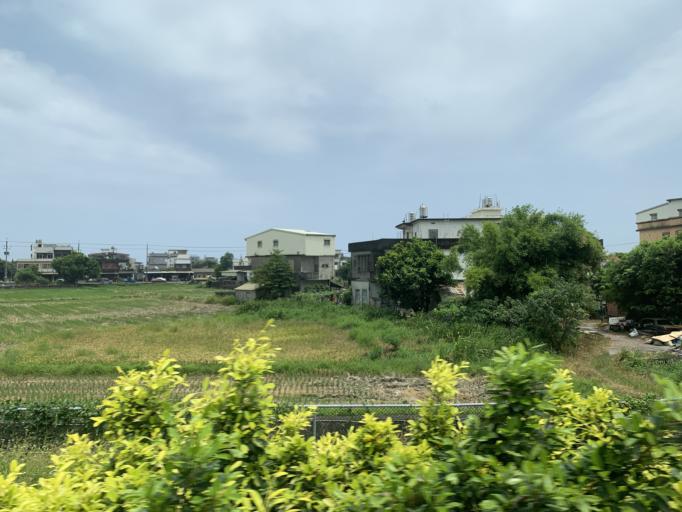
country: TW
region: Taiwan
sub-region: Yilan
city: Yilan
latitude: 24.8402
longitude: 121.8044
